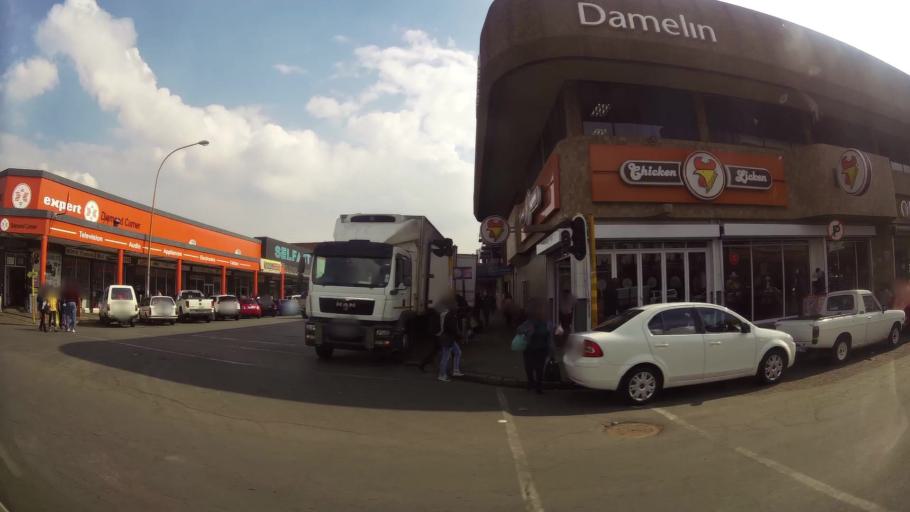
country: ZA
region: Gauteng
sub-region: Sedibeng District Municipality
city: Vereeniging
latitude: -26.6750
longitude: 27.9315
